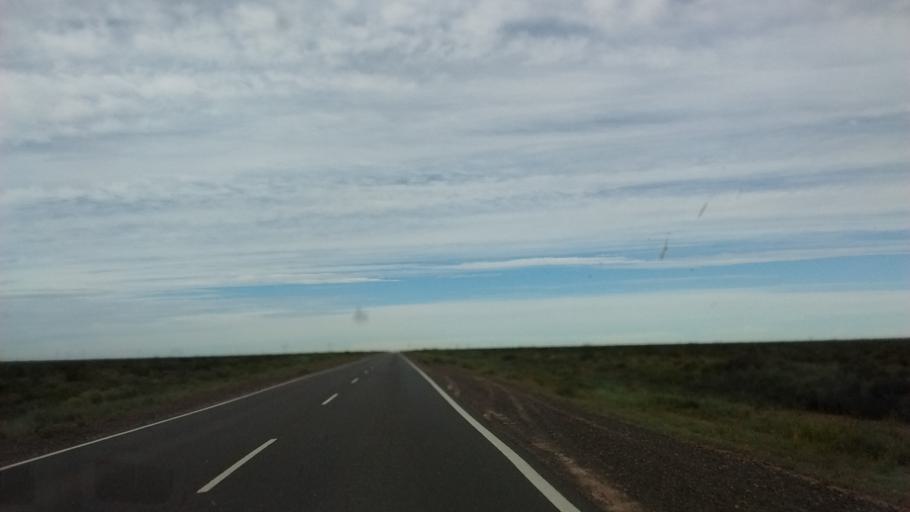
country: AR
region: Rio Negro
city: Contraalmirante Cordero
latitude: -38.5474
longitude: -68.0853
